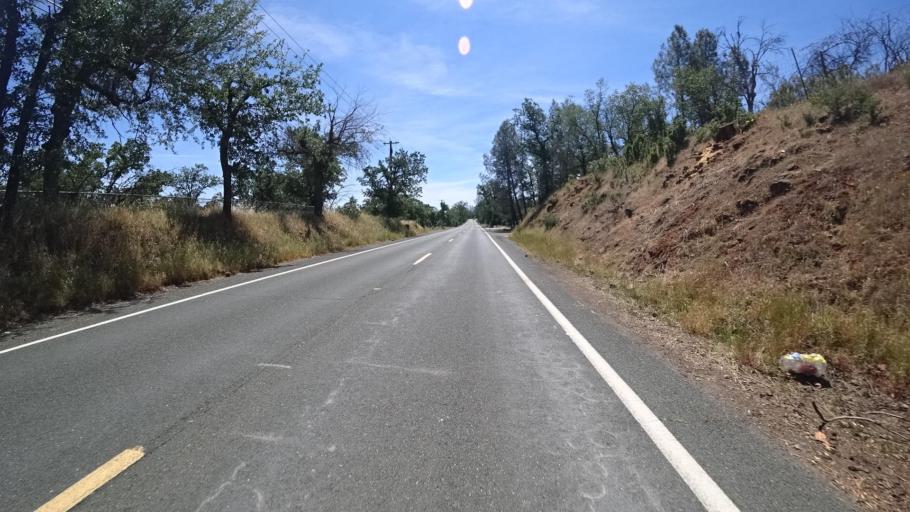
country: US
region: California
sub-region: Lake County
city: Middletown
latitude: 38.7537
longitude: -122.6006
